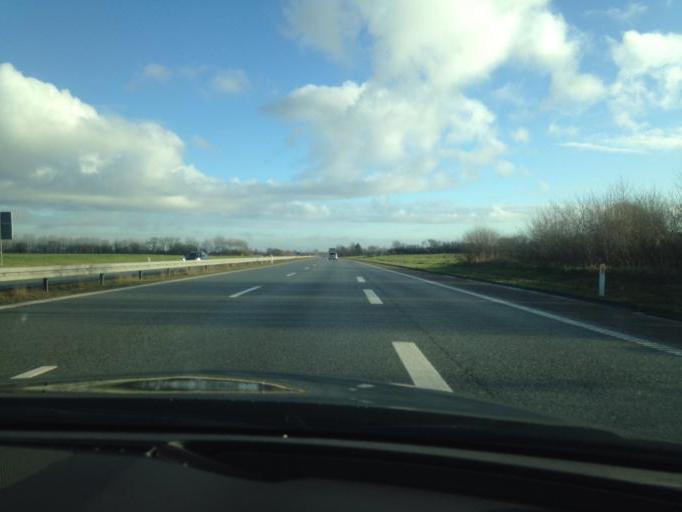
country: DK
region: South Denmark
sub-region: Vejen Kommune
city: Brorup
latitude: 55.5037
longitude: 9.0282
